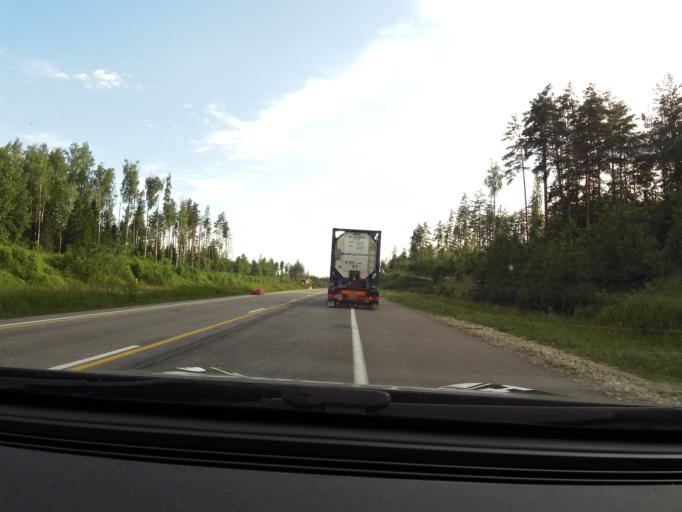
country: RU
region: Vladimir
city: Sudogda
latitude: 56.1206
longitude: 40.8561
